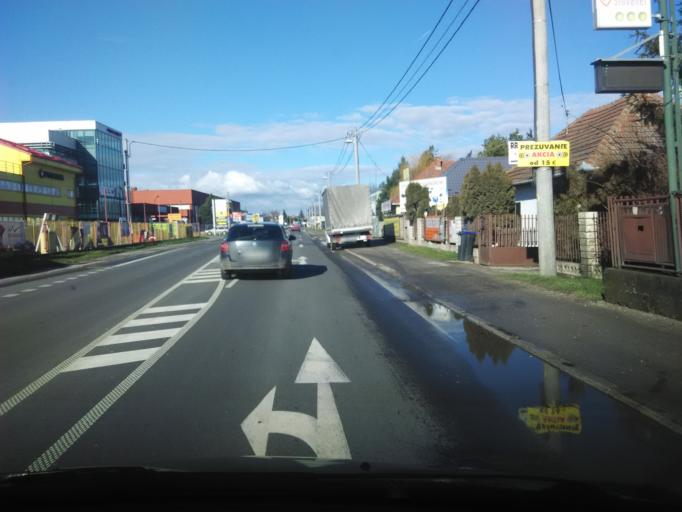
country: SK
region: Nitriansky
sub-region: Okres Nitra
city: Nitra
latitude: 48.2778
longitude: 18.0960
